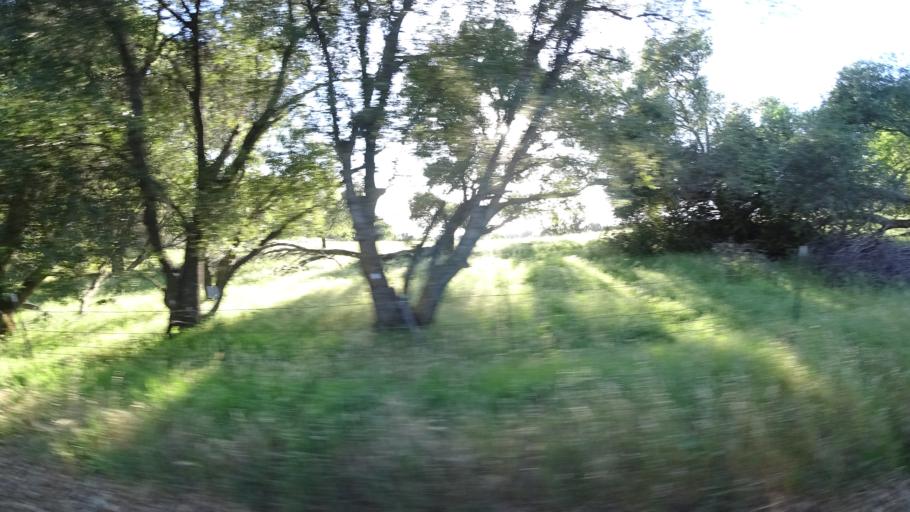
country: US
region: California
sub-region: Placer County
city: Lincoln
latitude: 38.9163
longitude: -121.2238
